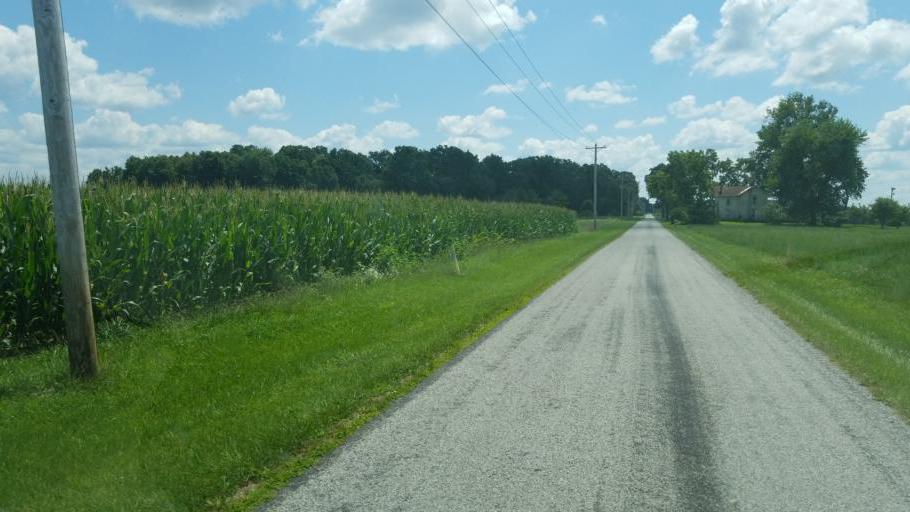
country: US
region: Ohio
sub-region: Marion County
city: Marion
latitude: 40.6663
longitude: -83.0923
